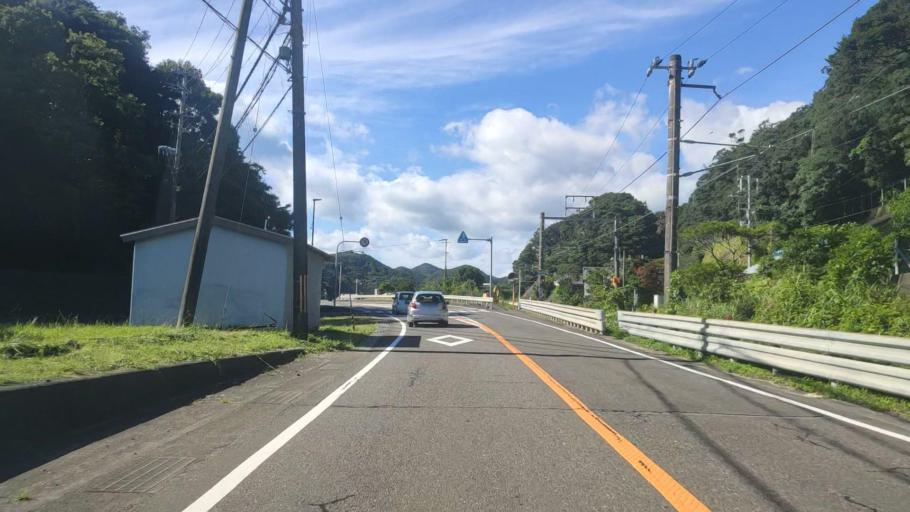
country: JP
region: Wakayama
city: Shingu
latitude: 33.4813
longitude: 135.7701
